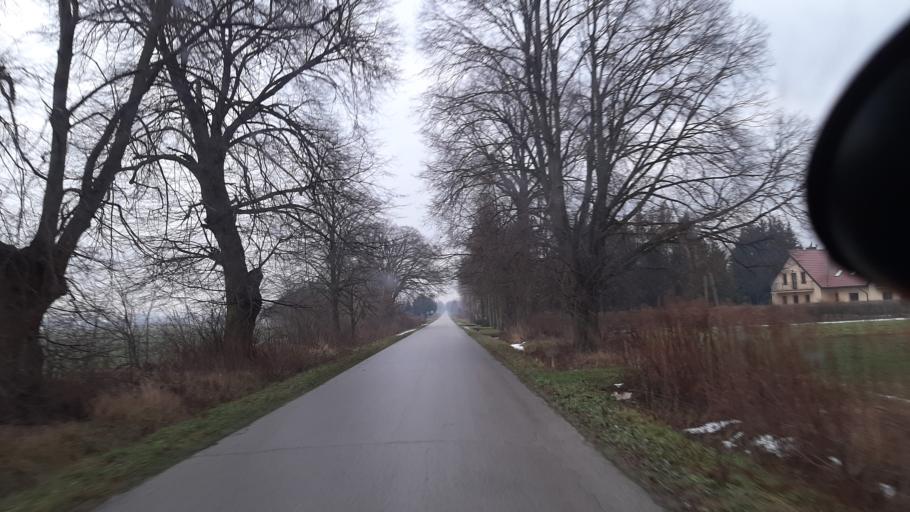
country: PL
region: Lublin Voivodeship
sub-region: Powiat lubelski
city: Lublin
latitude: 51.3400
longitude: 22.5373
